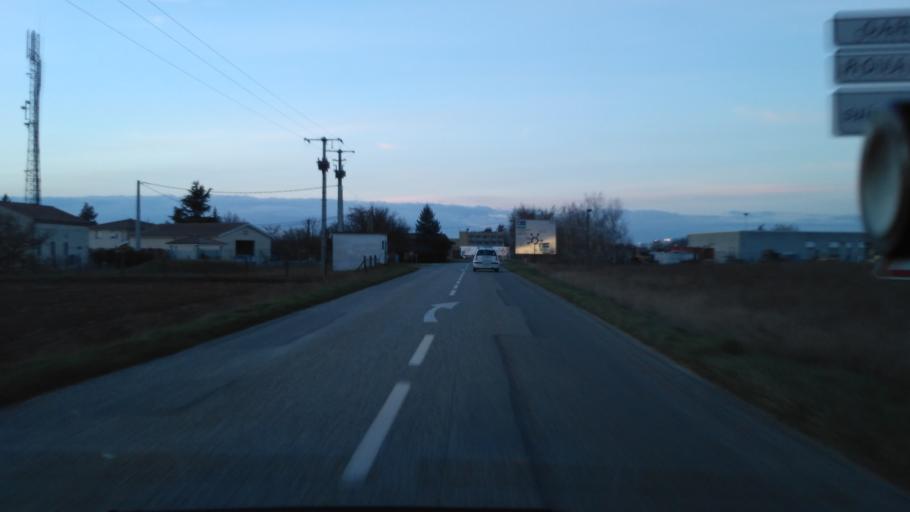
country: FR
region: Rhone-Alpes
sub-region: Departement de la Drome
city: Alixan
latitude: 44.9957
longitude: 5.0023
